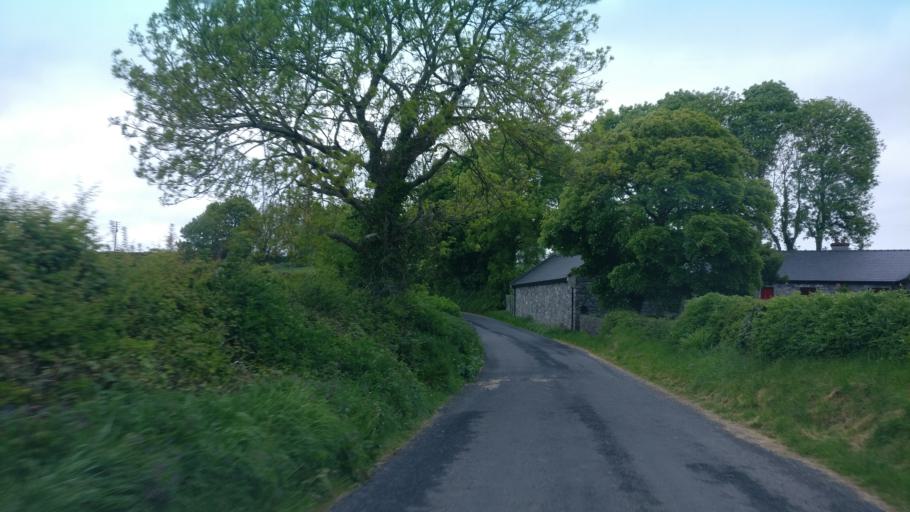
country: IE
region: Connaught
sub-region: County Galway
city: Portumna
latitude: 53.1209
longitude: -8.2900
